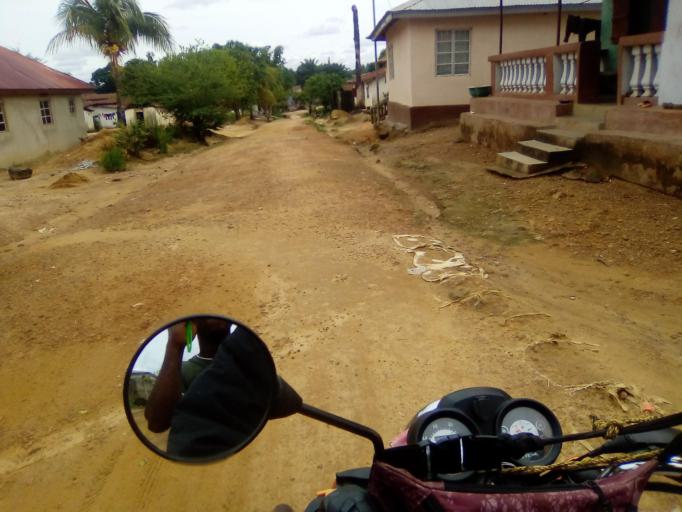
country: SL
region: Southern Province
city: Bo
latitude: 7.9417
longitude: -11.7302
